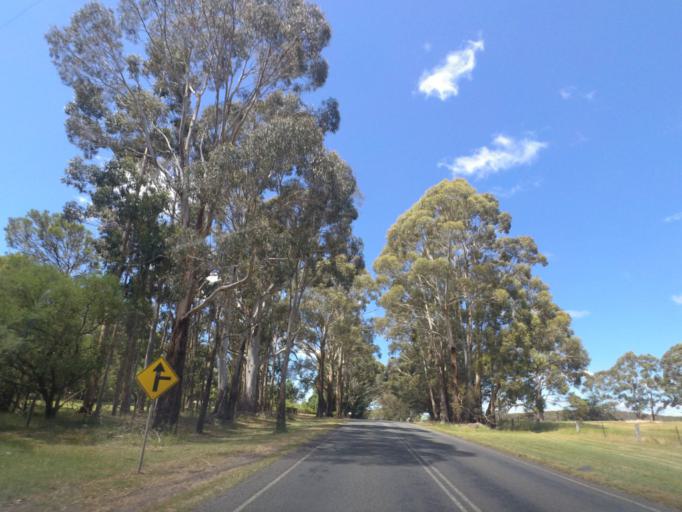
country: AU
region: Victoria
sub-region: Mount Alexander
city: Castlemaine
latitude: -37.3161
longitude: 144.2199
